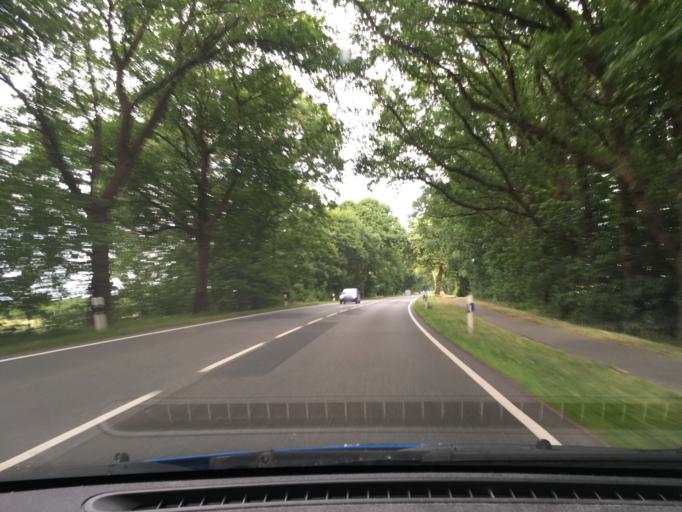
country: DE
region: Lower Saxony
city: Kakenstorf
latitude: 53.3159
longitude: 9.7733
